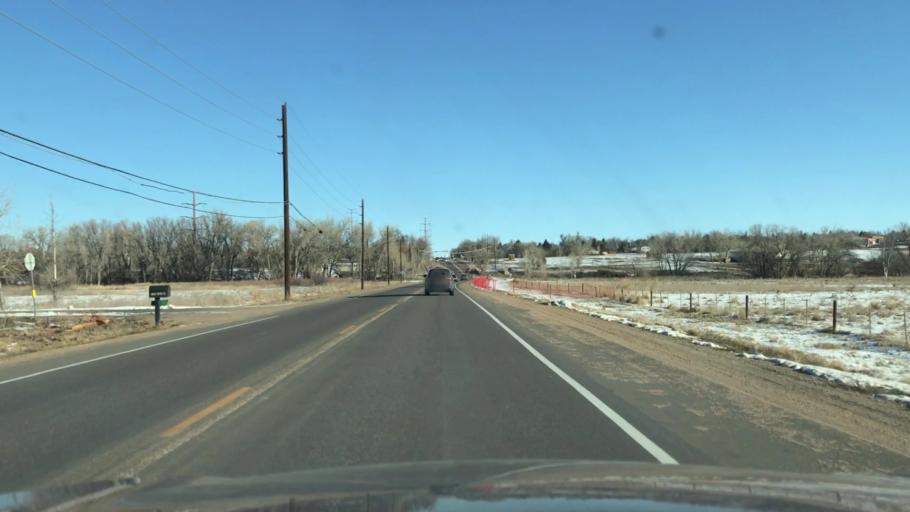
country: US
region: Colorado
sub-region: Boulder County
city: Gunbarrel
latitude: 40.0485
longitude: -105.1784
